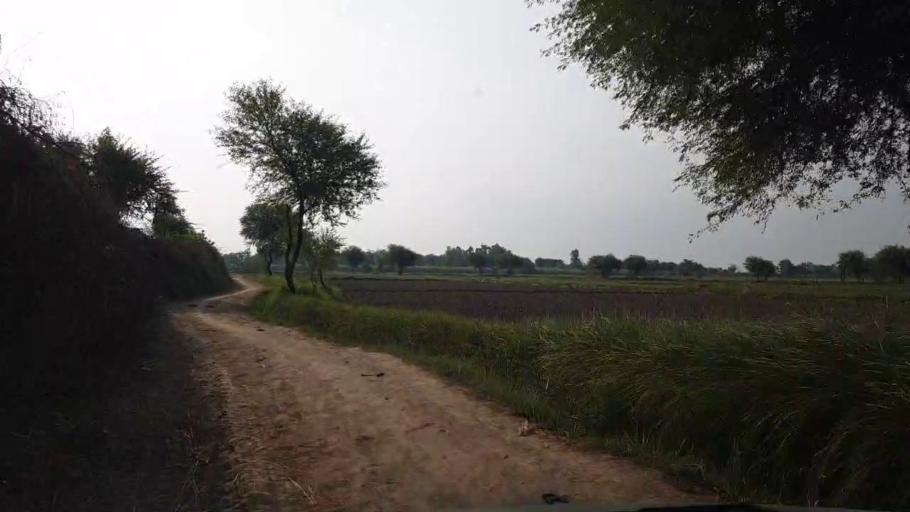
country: PK
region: Sindh
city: Rajo Khanani
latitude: 24.9075
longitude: 68.9204
